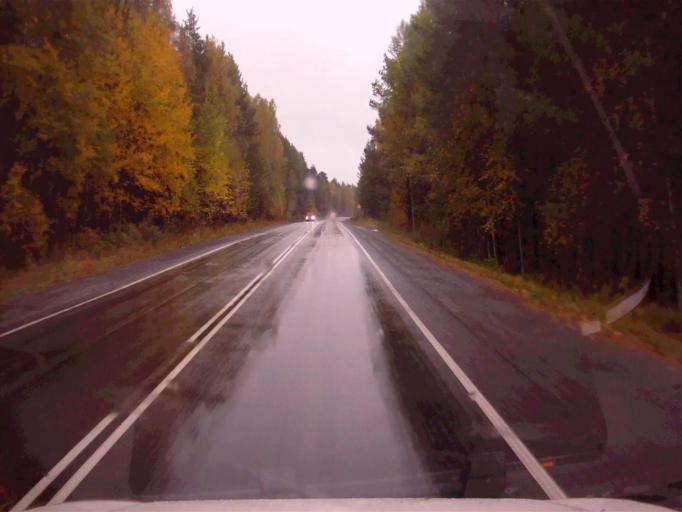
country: RU
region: Chelyabinsk
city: Tayginka
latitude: 55.5545
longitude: 60.6462
